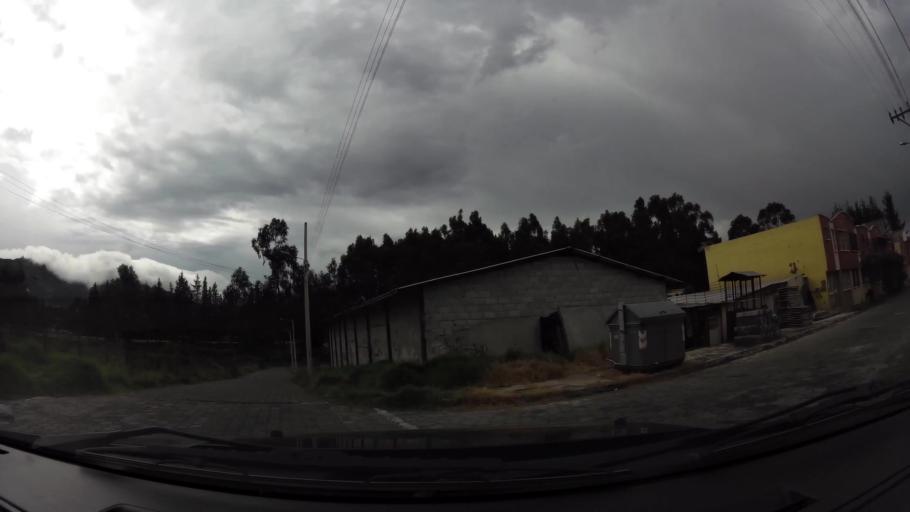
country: EC
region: Pichincha
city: Quito
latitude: -0.2889
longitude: -78.5534
